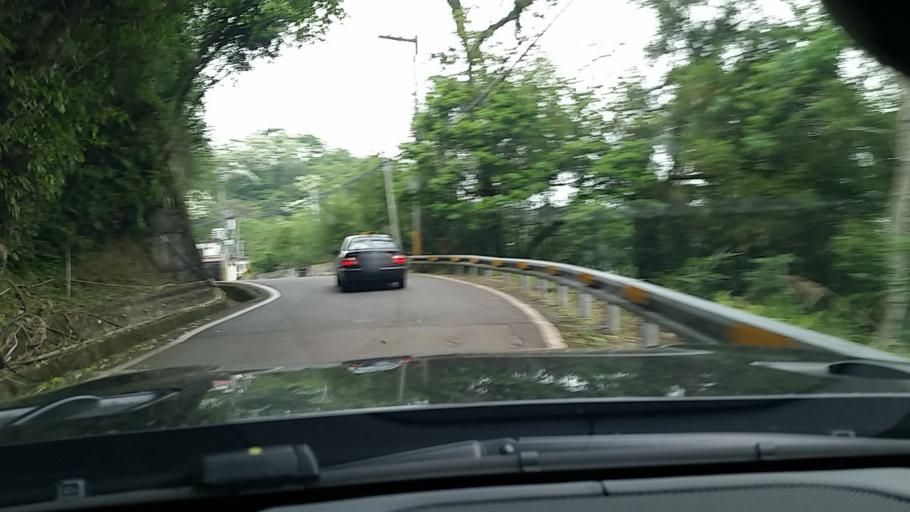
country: TW
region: Taiwan
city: Daxi
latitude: 24.7985
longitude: 121.2846
